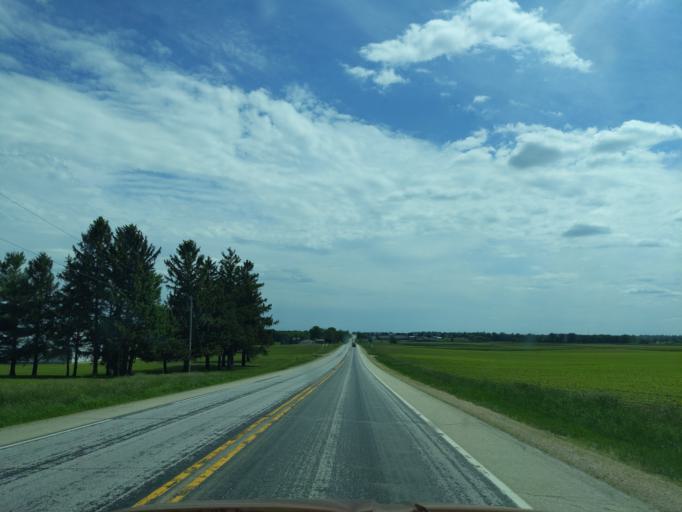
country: US
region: Wisconsin
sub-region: Dane County
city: De Forest
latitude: 43.2855
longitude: -89.3248
